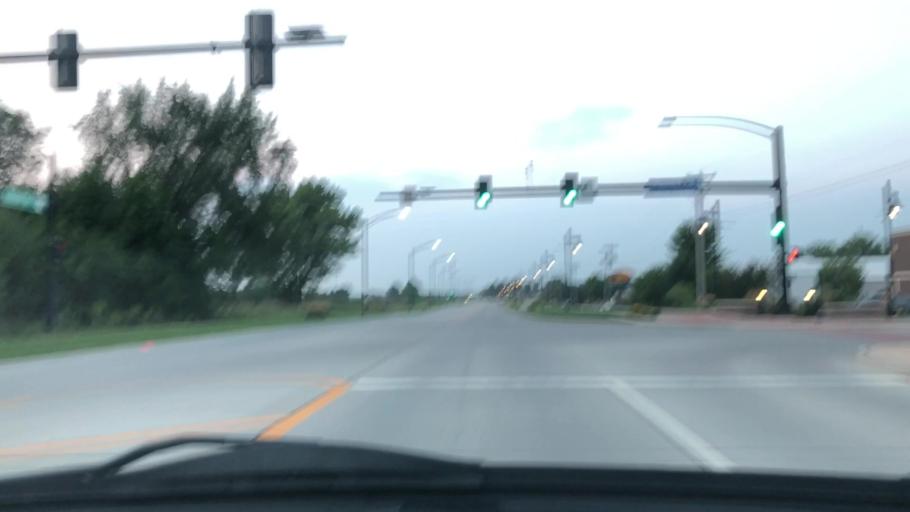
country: US
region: Iowa
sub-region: Johnson County
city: North Liberty
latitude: 41.7536
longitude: -91.6075
